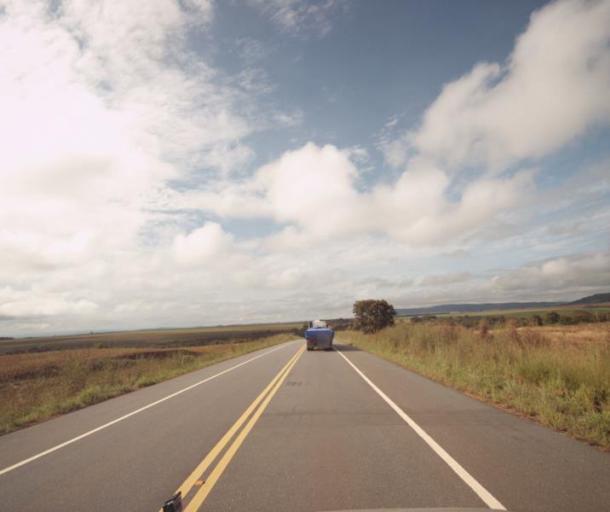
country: BR
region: Goias
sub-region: Barro Alto
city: Barro Alto
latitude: -15.2736
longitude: -48.6840
